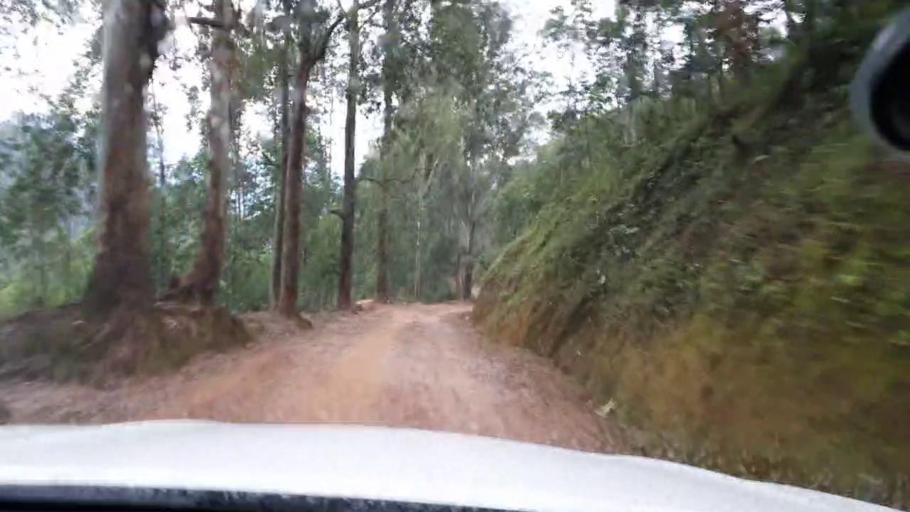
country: RW
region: Western Province
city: Cyangugu
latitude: -2.4098
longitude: 29.1992
